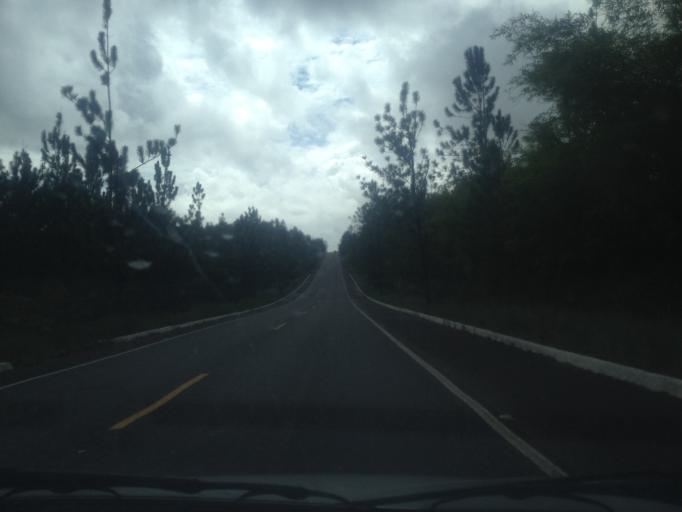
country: BR
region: Bahia
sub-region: Entre Rios
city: Entre Rios
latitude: -12.1277
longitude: -37.7909
